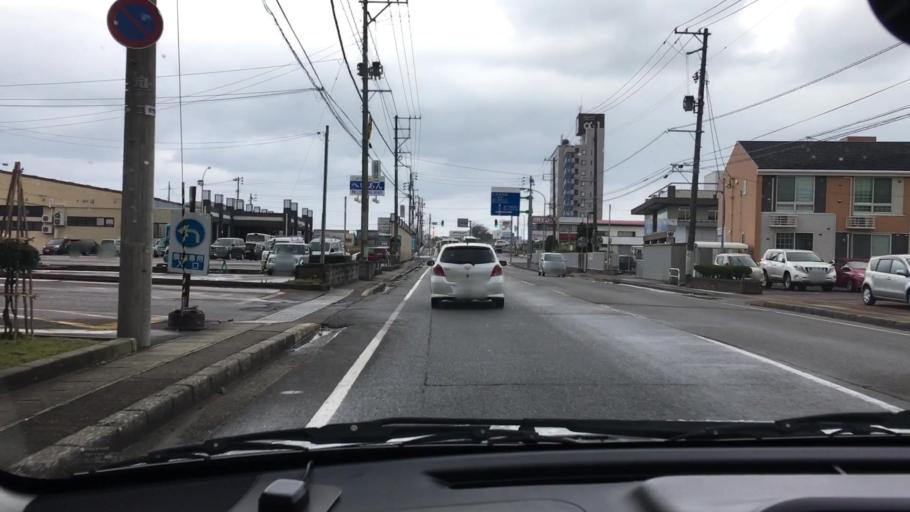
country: JP
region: Niigata
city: Joetsu
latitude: 37.1640
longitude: 138.2373
